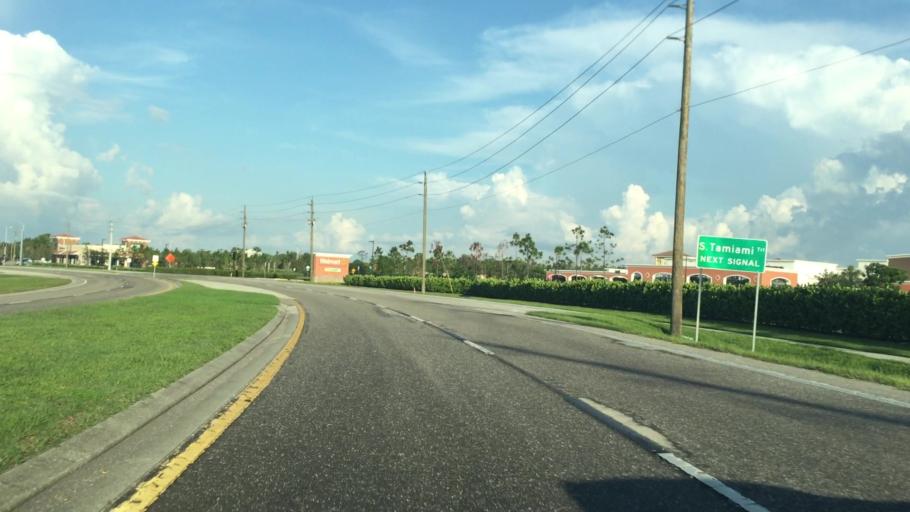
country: US
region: Florida
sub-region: Lee County
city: Estero
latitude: 26.4497
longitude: -81.8148
